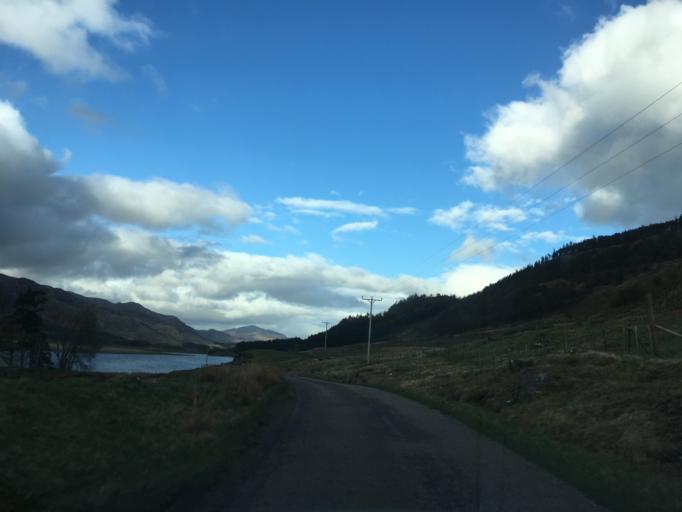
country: GB
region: Scotland
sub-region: Highland
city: Kingussie
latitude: 57.0044
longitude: -4.3618
